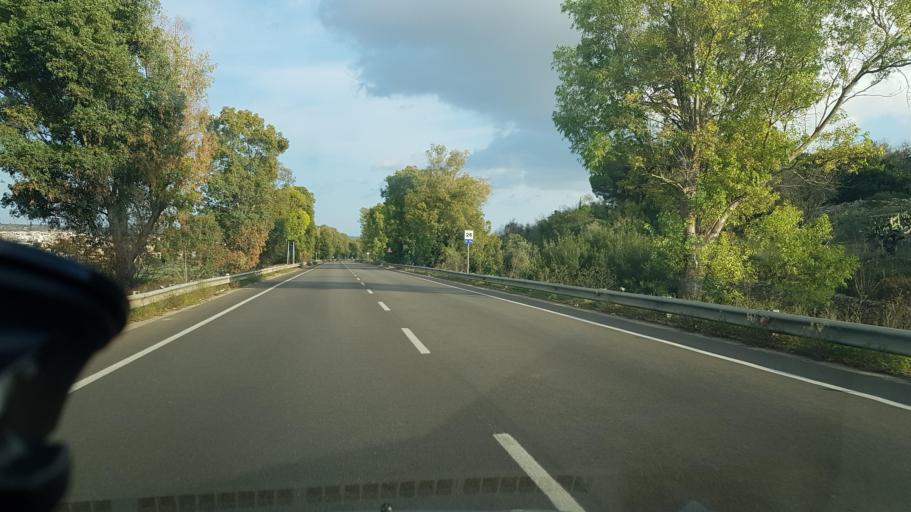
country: IT
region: Apulia
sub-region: Provincia di Lecce
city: Acquarica del Capo
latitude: 39.9064
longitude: 18.2400
